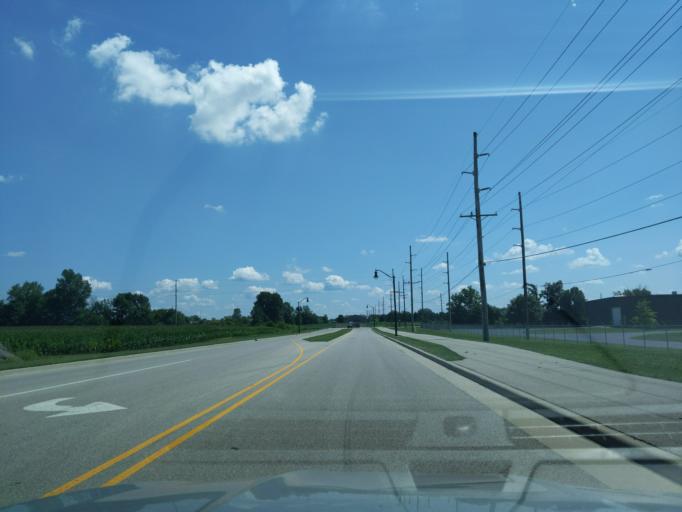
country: US
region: Indiana
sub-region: Decatur County
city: Greensburg
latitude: 39.3586
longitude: -85.4914
